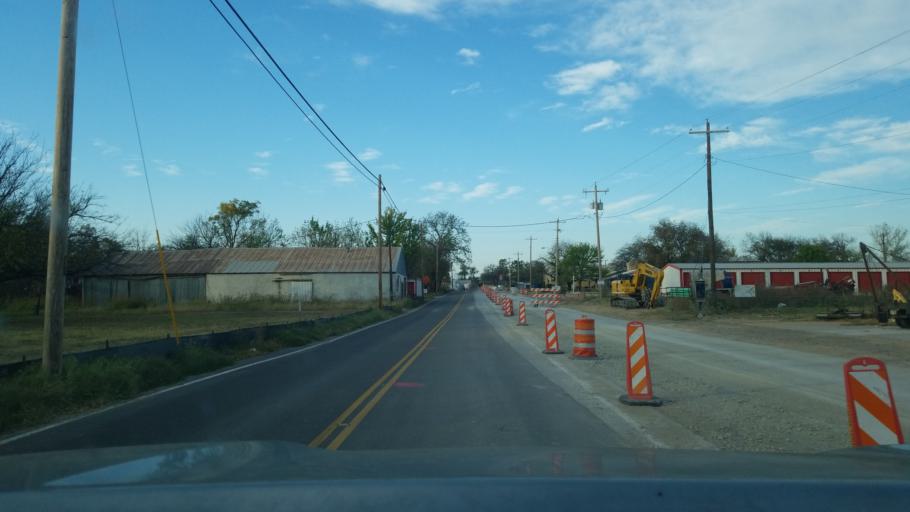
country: US
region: Texas
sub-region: Brown County
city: Lake Brownwood
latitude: 32.0970
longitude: -98.9640
